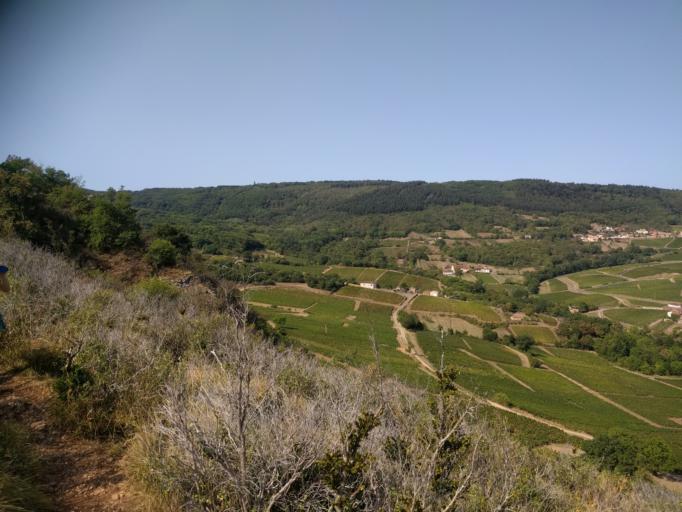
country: FR
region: Bourgogne
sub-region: Departement de Saone-et-Loire
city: Prisse
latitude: 46.3030
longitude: 4.7220
